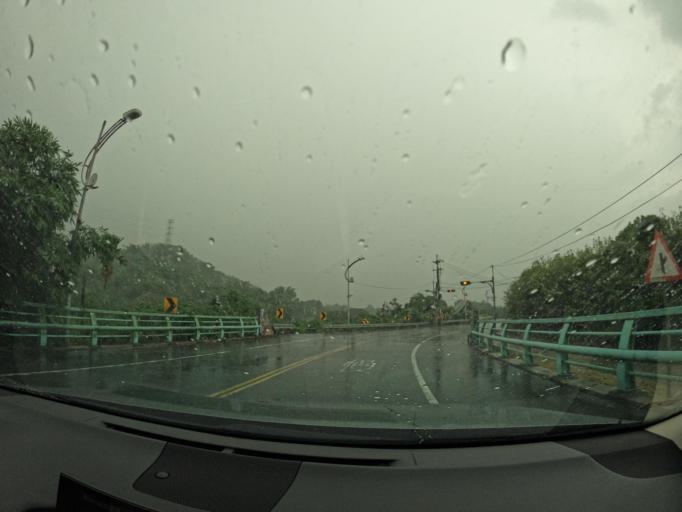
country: TW
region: Taiwan
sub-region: Nantou
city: Nantou
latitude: 23.8925
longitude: 120.7223
